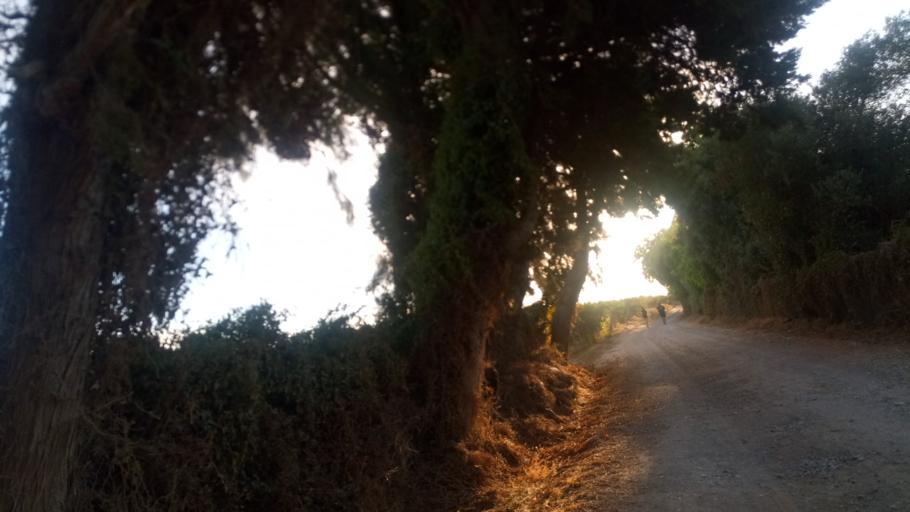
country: PT
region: Faro
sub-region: Tavira
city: Tavira
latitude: 37.1473
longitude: -7.5903
